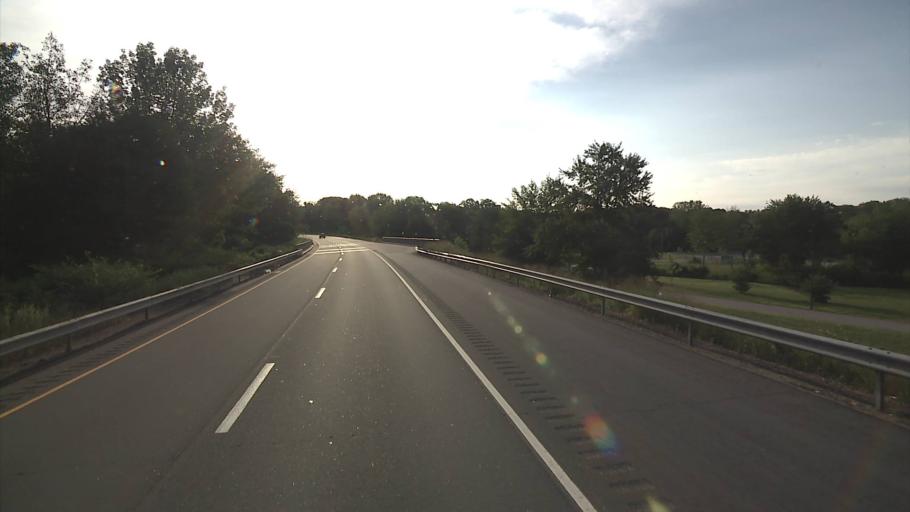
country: US
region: Connecticut
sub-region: New London County
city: Colchester
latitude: 41.5618
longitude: -72.3206
